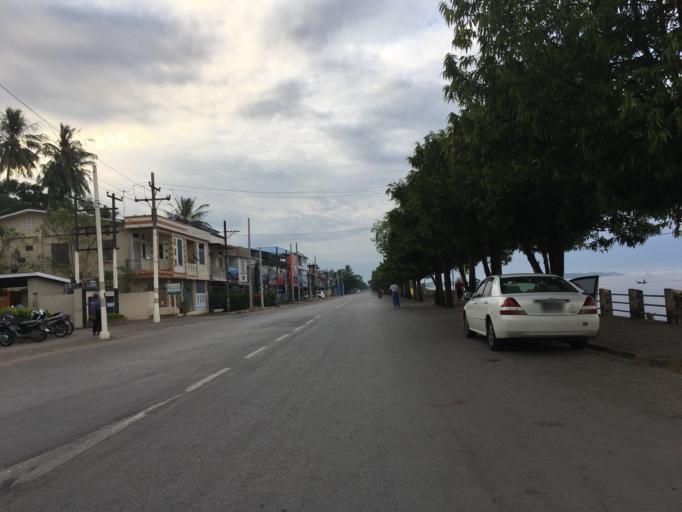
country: MM
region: Mon
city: Mawlamyine
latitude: 16.4783
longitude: 97.6194
